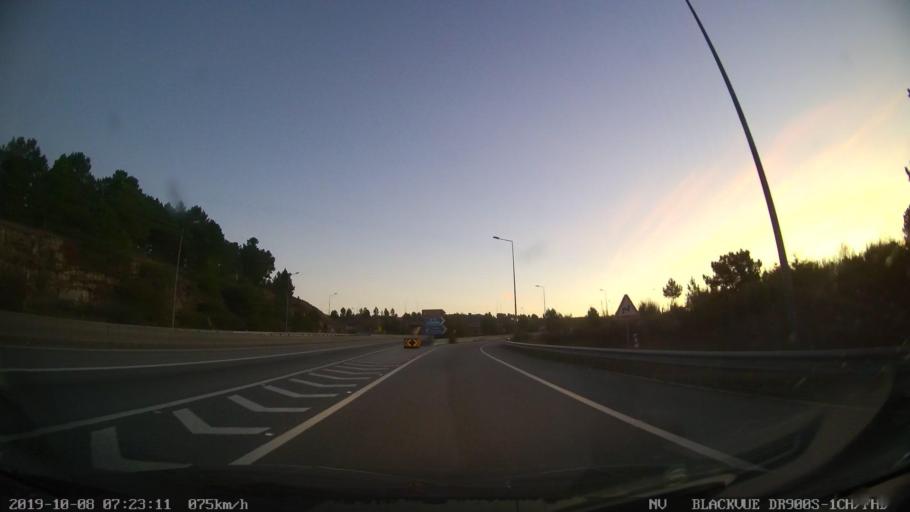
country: PT
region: Vila Real
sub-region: Vila Real
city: Vila Real
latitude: 41.3217
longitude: -7.7018
